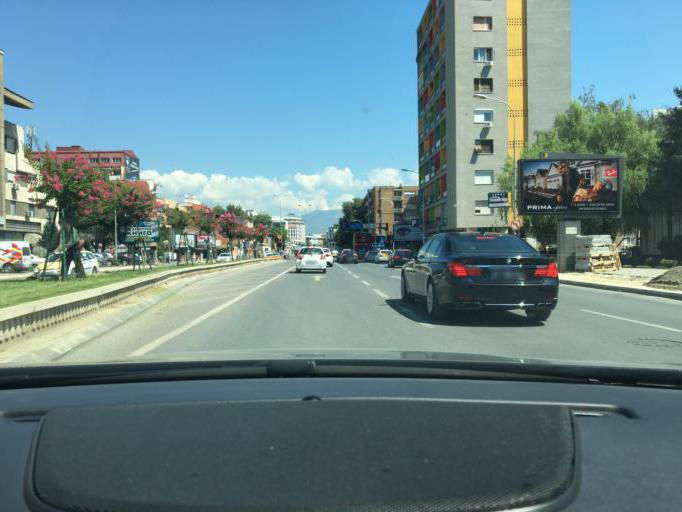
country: MK
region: Karpos
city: Skopje
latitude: 41.9943
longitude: 21.4247
